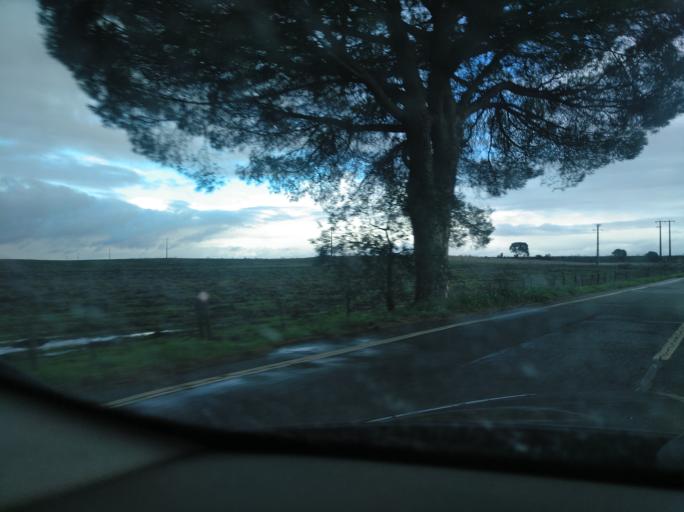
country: PT
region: Beja
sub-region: Aljustrel
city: Aljustrel
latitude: 37.9315
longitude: -8.3475
